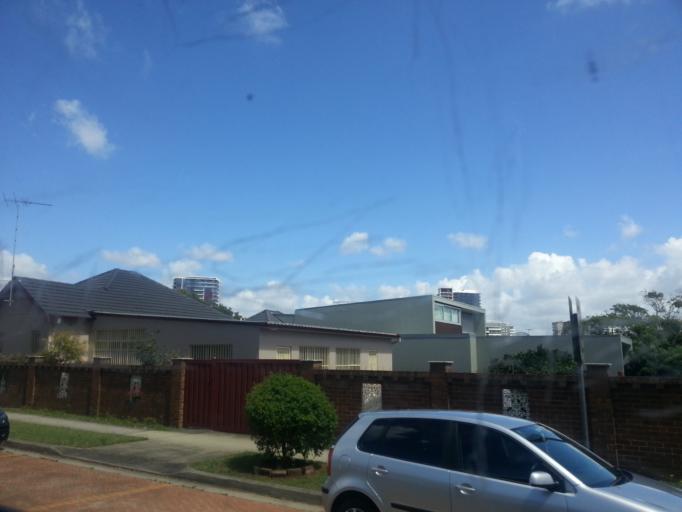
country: AU
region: New South Wales
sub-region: Randwick
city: Kensington
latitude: -33.9103
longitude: 151.2176
